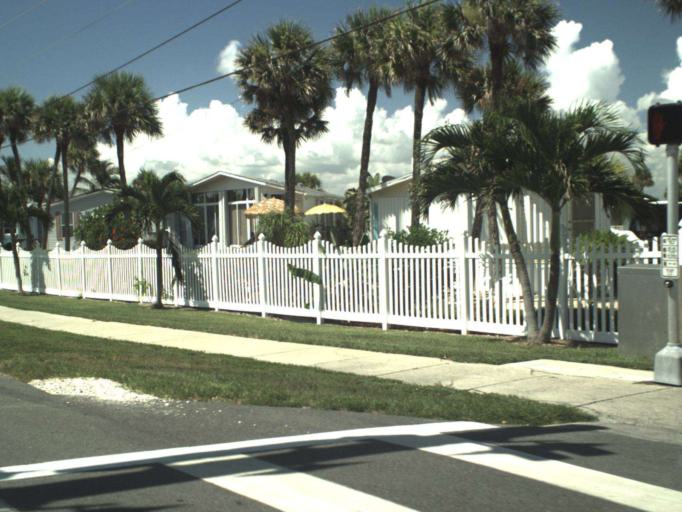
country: US
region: Florida
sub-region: Indian River County
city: South Beach
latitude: 27.5315
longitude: -80.3144
